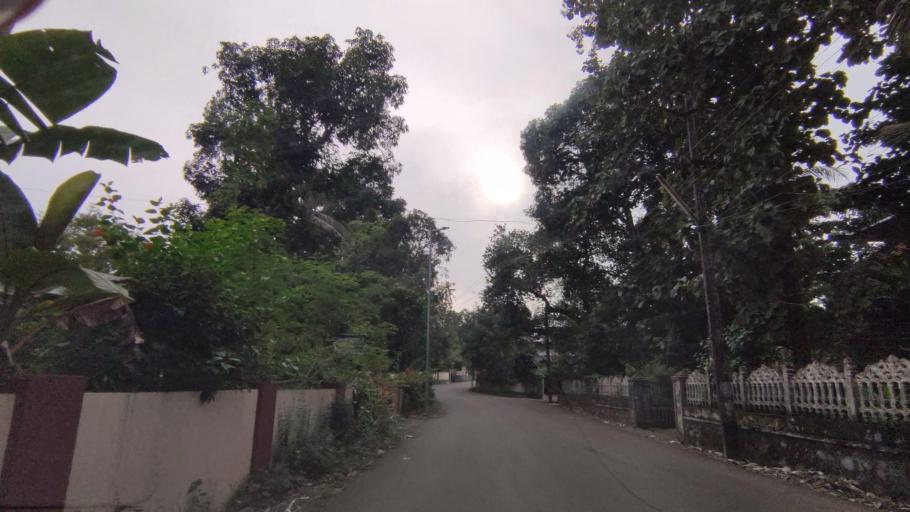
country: IN
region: Kerala
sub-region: Kottayam
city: Kottayam
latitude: 9.6637
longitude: 76.5231
